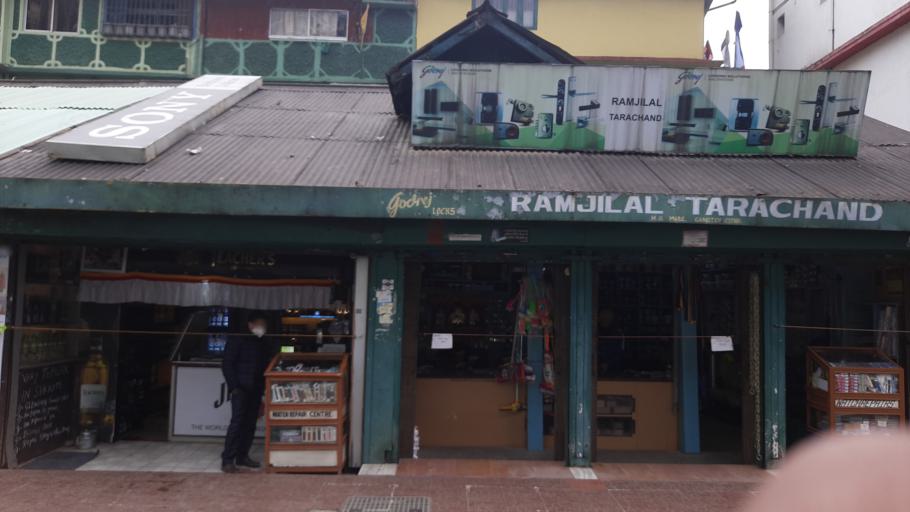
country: IN
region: Sikkim
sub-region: East District
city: Gangtok
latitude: 27.3280
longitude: 88.6127
